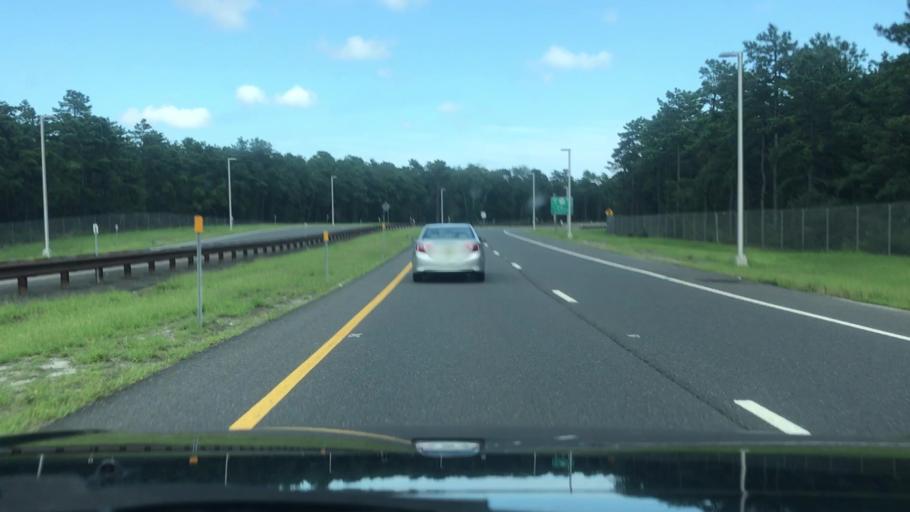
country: US
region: New Jersey
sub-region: Ocean County
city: Leisure Village
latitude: 40.0573
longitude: -74.1640
